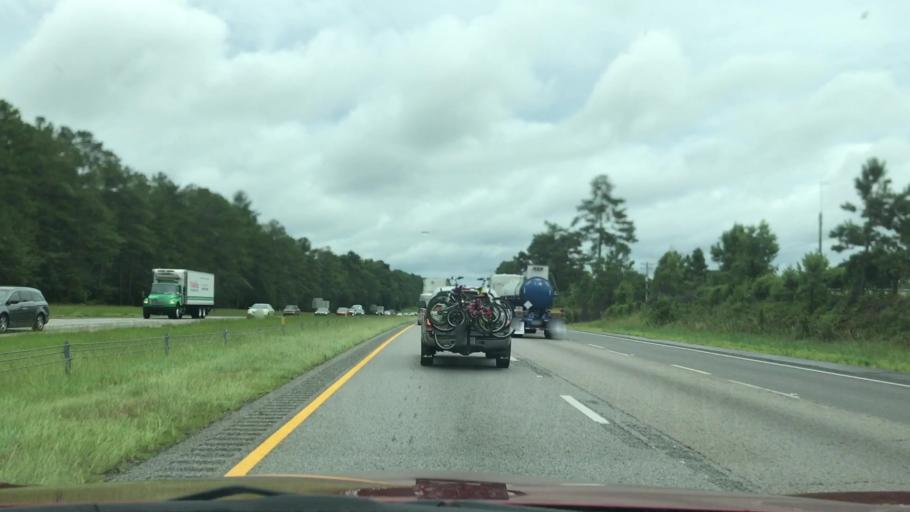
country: US
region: South Carolina
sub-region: Orangeburg County
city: Brookdale
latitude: 33.5556
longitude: -80.8213
